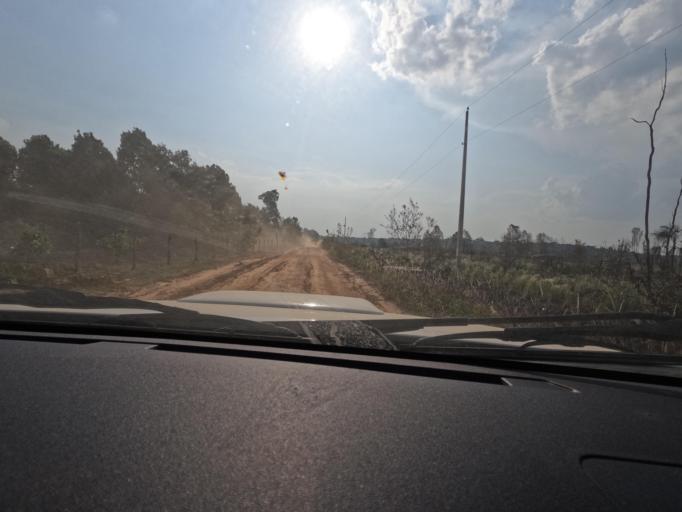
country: BR
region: Rondonia
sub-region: Porto Velho
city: Porto Velho
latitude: -8.5728
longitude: -64.0171
